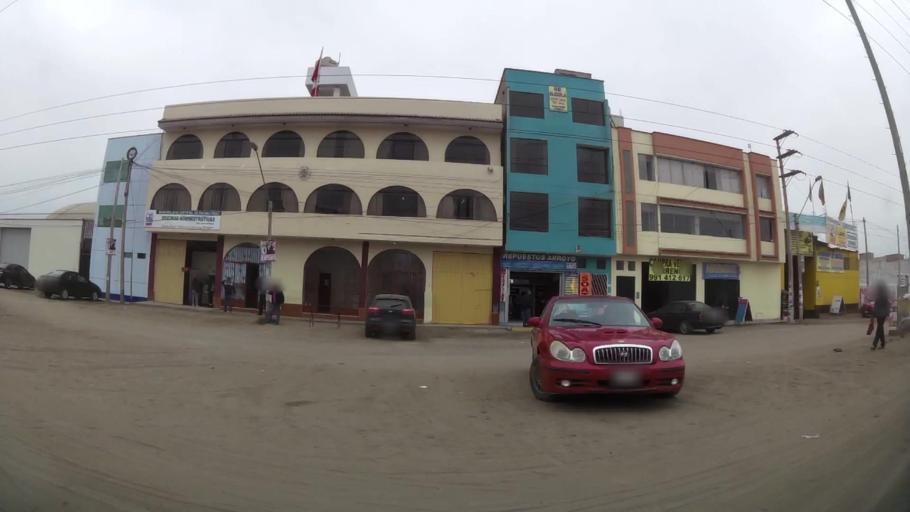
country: PE
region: Lima
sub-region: Lima
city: Punta Hermosa
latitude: -12.2560
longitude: -76.8894
